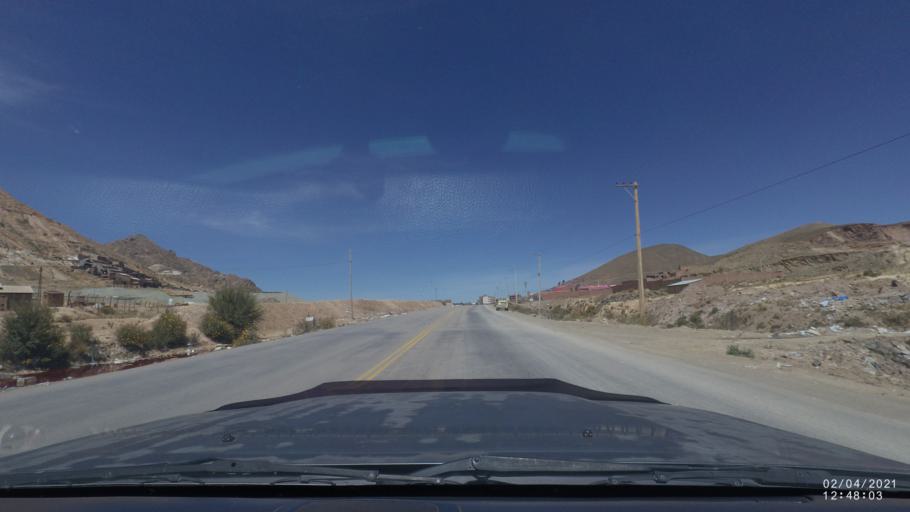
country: BO
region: Oruro
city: Oruro
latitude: -17.9601
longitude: -67.1424
